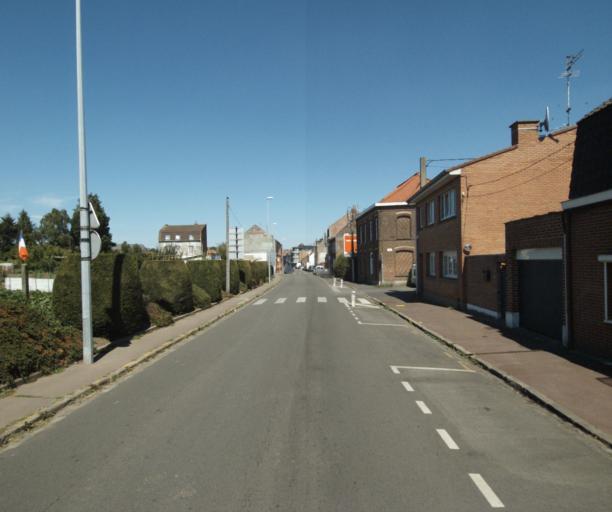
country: BE
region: Wallonia
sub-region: Province du Hainaut
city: Mouscron
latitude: 50.7358
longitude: 3.1951
